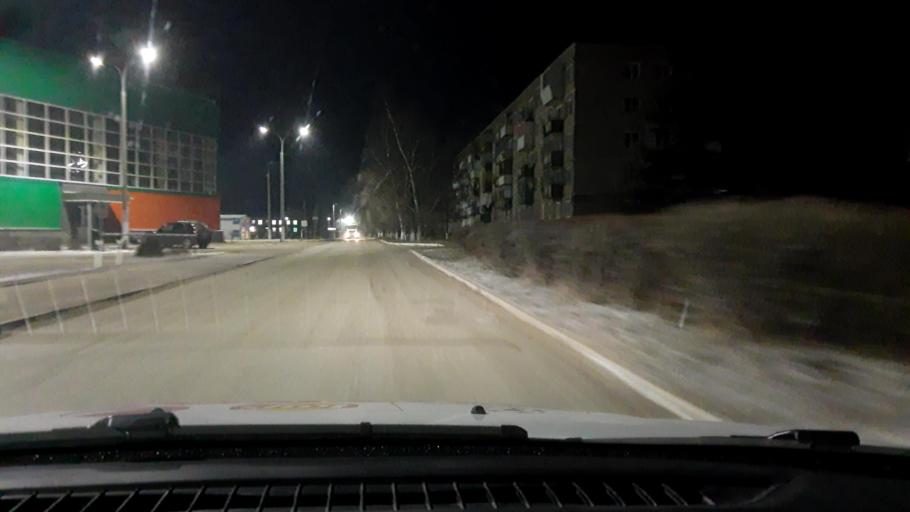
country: RU
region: Nizjnij Novgorod
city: Volodarsk
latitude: 56.2399
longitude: 43.1862
